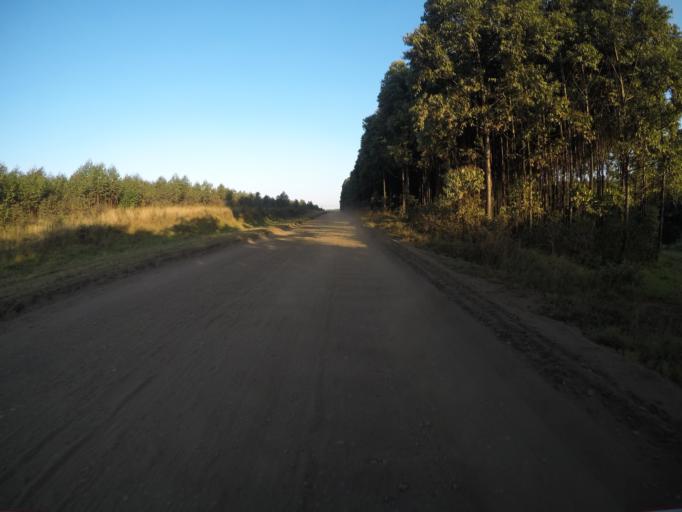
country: ZA
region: KwaZulu-Natal
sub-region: uThungulu District Municipality
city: KwaMbonambi
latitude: -28.6783
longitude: 32.1200
